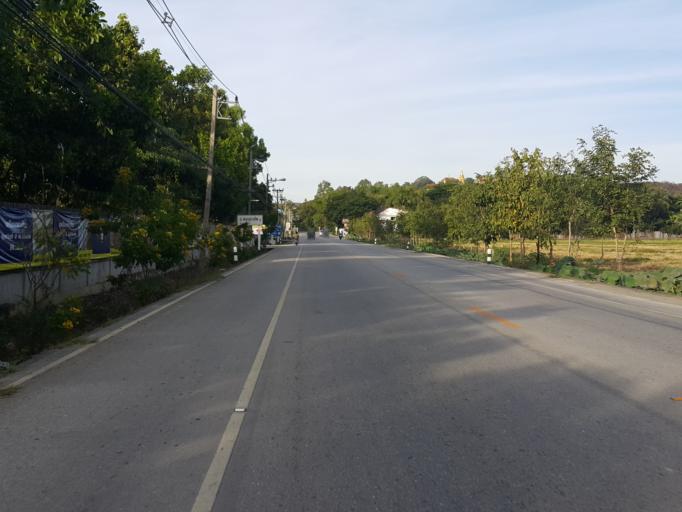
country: TH
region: Chiang Mai
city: San Sai
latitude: 18.8634
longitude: 99.1344
